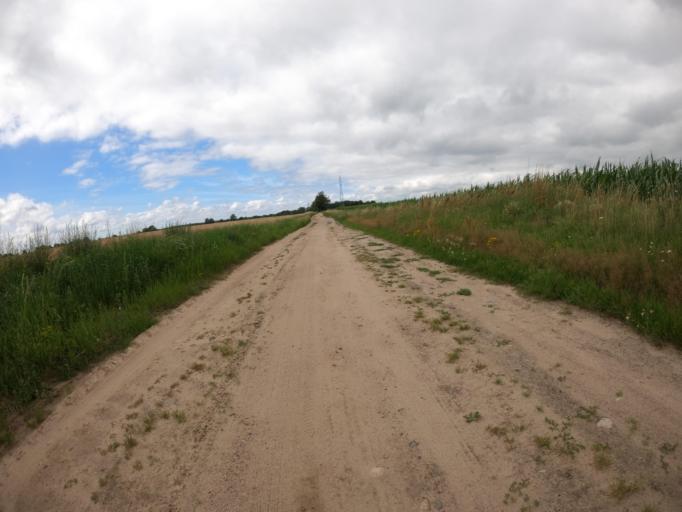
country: PL
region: West Pomeranian Voivodeship
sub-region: Powiat bialogardzki
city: Tychowo
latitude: 53.9960
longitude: 16.3778
